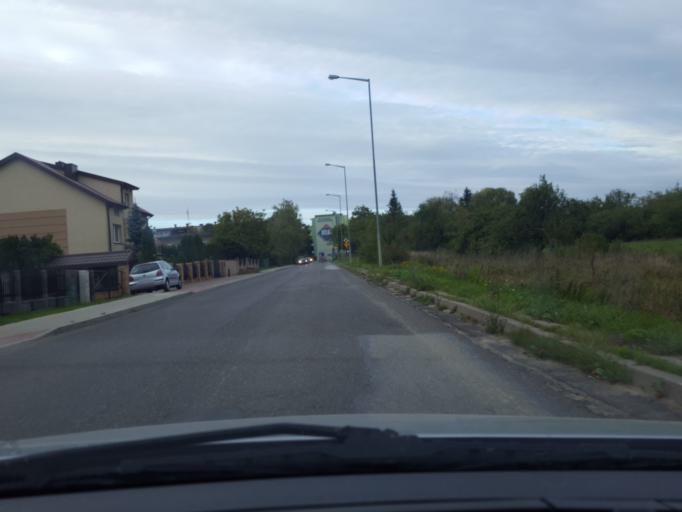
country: PL
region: Lodz Voivodeship
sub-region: Powiat brzezinski
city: Brzeziny
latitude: 51.7982
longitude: 19.7625
